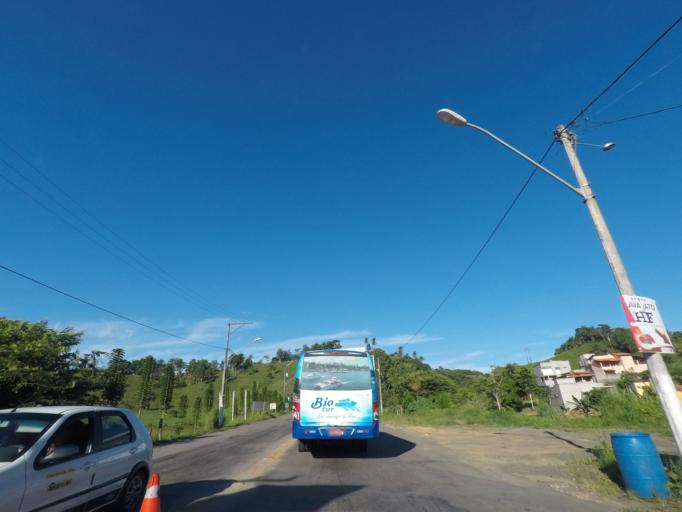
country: BR
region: Bahia
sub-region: Nazare
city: Nazare
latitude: -13.0302
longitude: -39.0150
